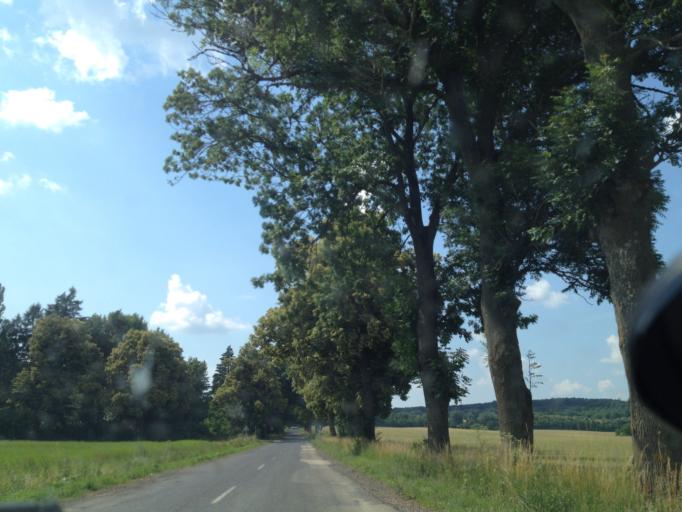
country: HU
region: Veszprem
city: Urkut
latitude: 47.0741
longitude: 17.6846
